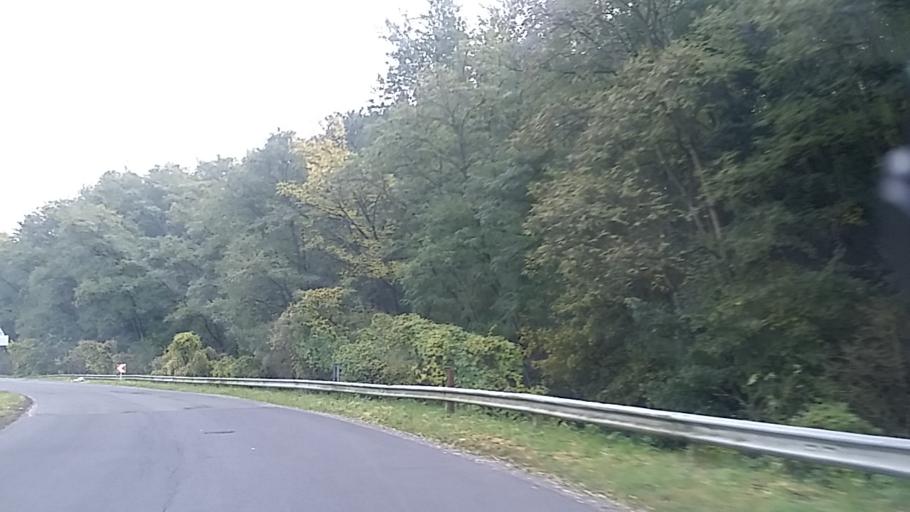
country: HU
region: Borsod-Abauj-Zemplen
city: Sajokaza
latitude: 48.2722
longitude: 20.5292
